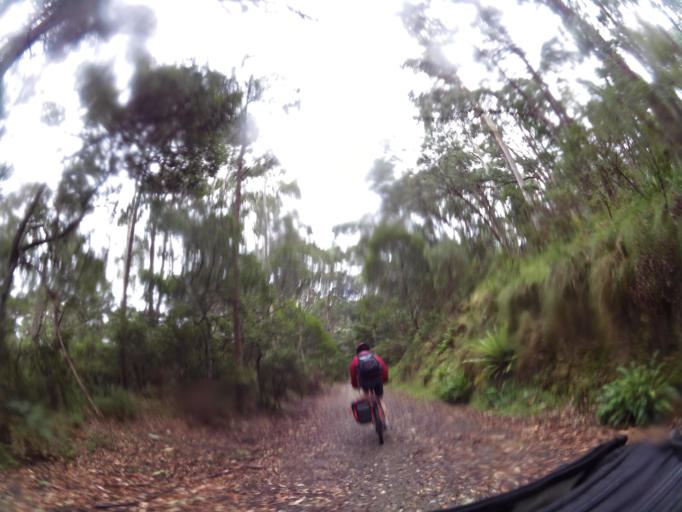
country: AU
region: New South Wales
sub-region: Greater Hume Shire
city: Holbrook
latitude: -36.1951
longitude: 147.5207
